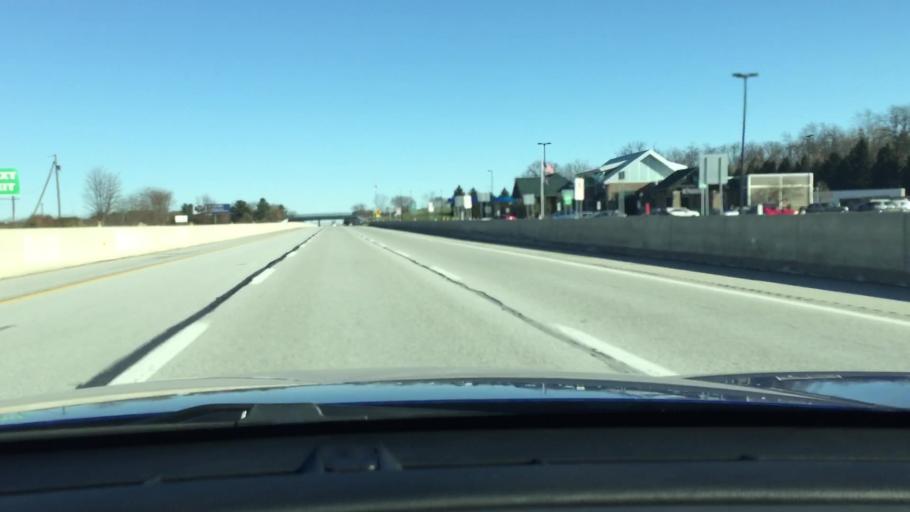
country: US
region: Pennsylvania
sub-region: Cumberland County
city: Carlisle
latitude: 40.2056
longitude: -77.2893
